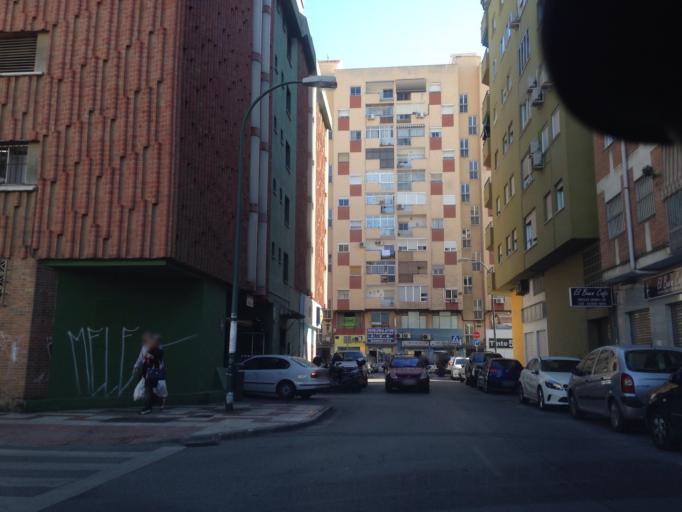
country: ES
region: Andalusia
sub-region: Provincia de Malaga
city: Malaga
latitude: 36.7057
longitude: -4.4391
